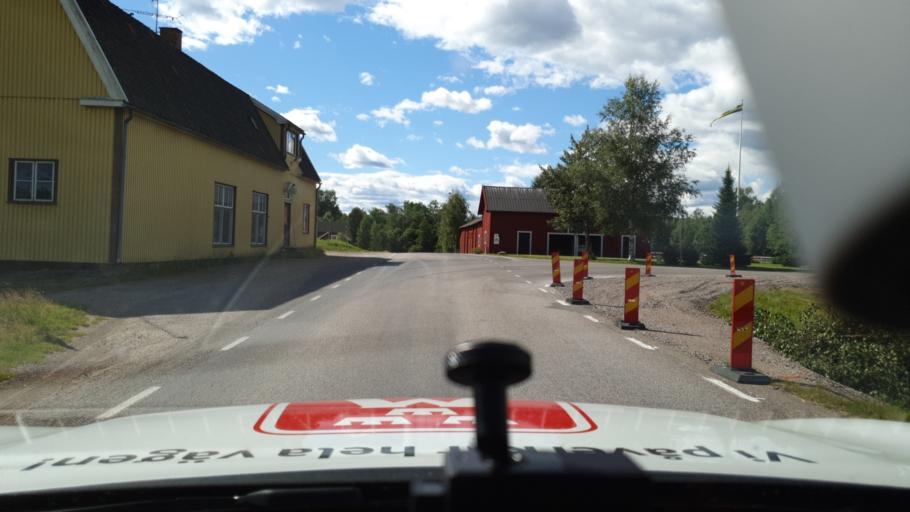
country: SE
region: Vaermland
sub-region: Torsby Kommun
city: Torsby
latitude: 59.9836
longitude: 12.8748
